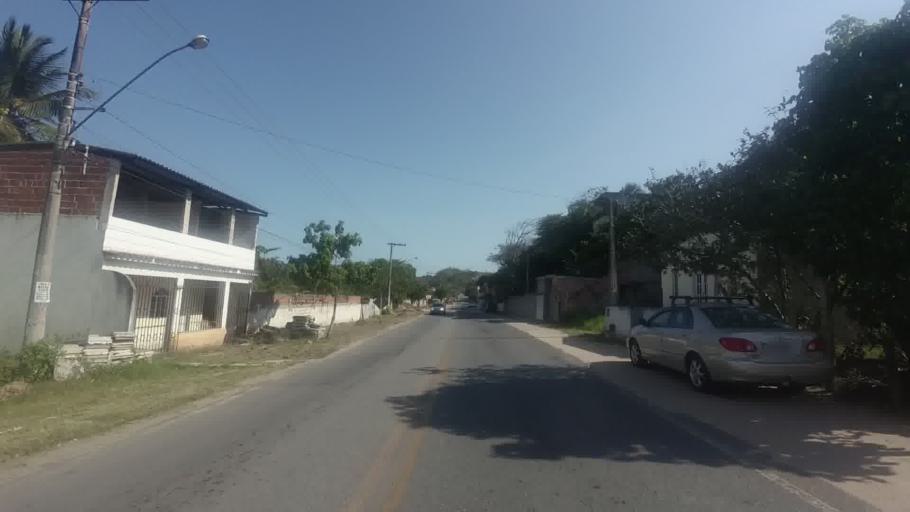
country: BR
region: Espirito Santo
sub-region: Piuma
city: Piuma
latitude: -20.8615
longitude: -40.7585
